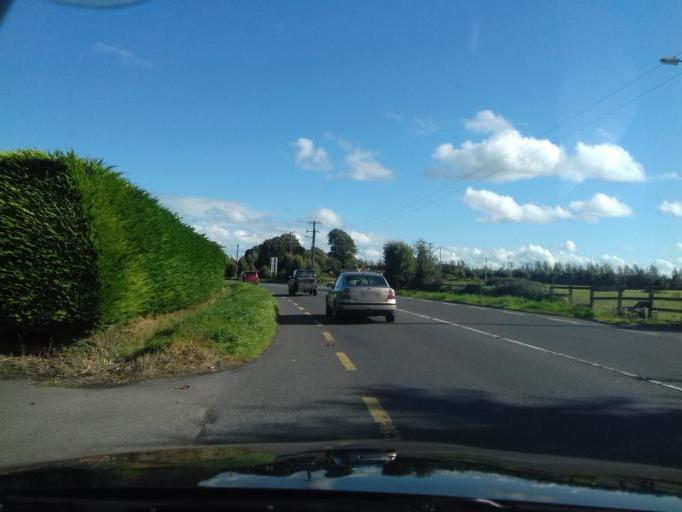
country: IE
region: Leinster
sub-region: Uibh Fhaili
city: Tullamore
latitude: 53.2563
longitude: -7.4820
